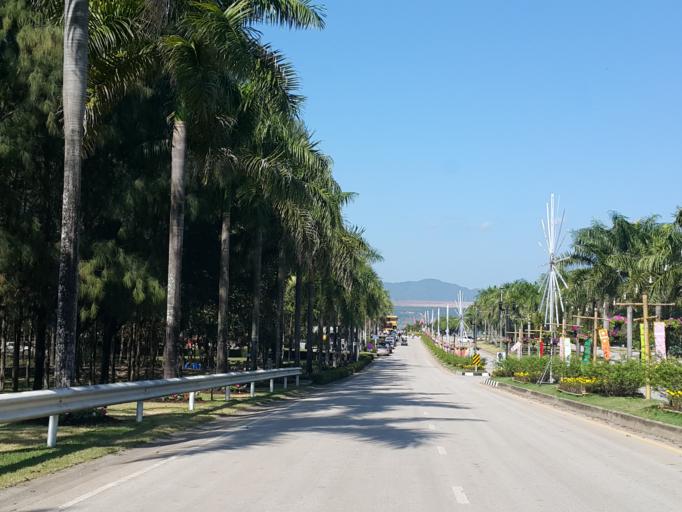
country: TH
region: Lampang
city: Mae Mo
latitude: 18.3170
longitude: 99.7452
